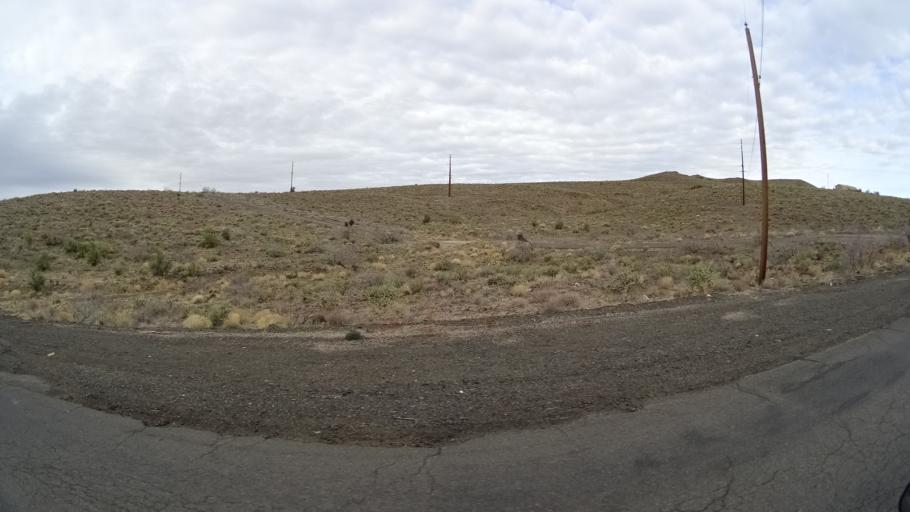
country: US
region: Arizona
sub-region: Mohave County
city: Kingman
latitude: 35.2119
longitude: -114.0785
